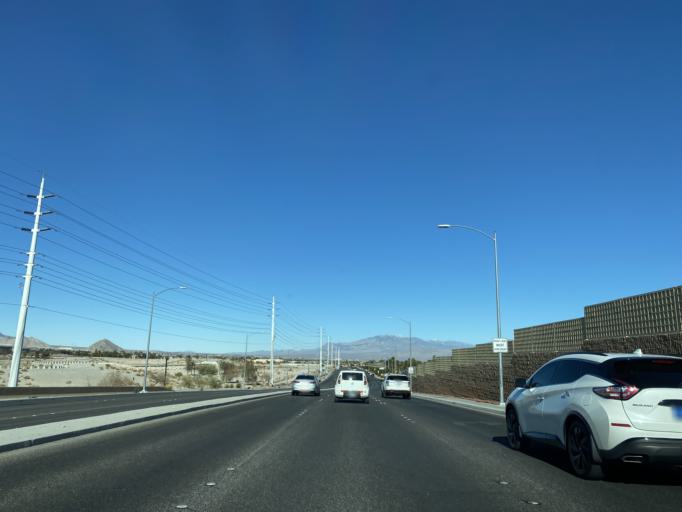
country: US
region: Nevada
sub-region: Clark County
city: Spring Valley
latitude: 36.1787
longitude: -115.2782
